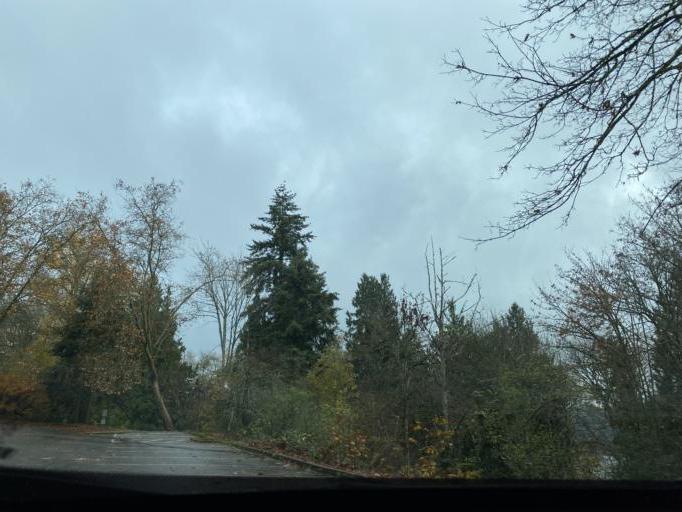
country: US
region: Washington
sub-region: King County
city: Mercer Island
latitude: 47.5332
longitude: -122.2163
